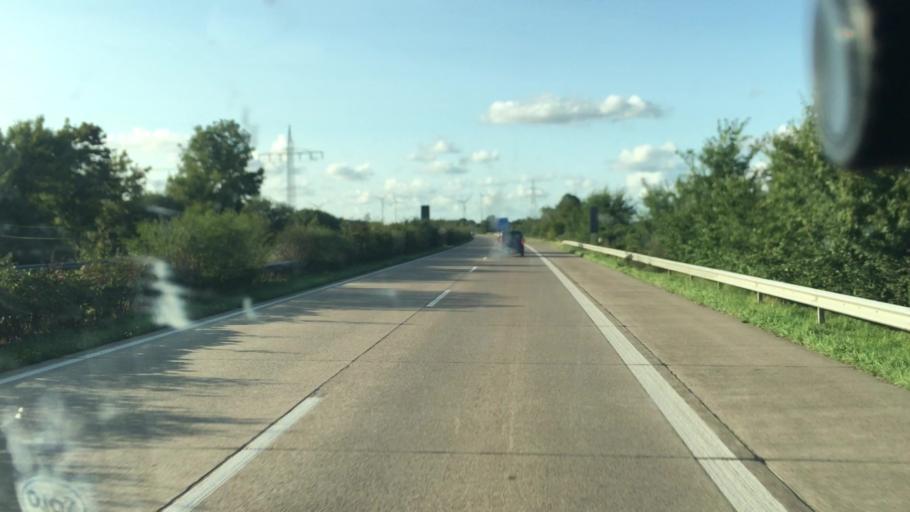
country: DE
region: Lower Saxony
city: Sande
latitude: 53.4765
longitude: 8.0138
